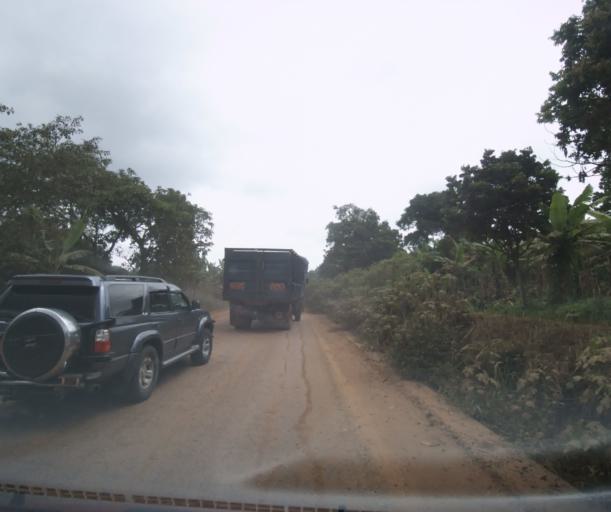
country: CM
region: West
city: Mbouda
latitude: 5.6671
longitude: 10.2192
